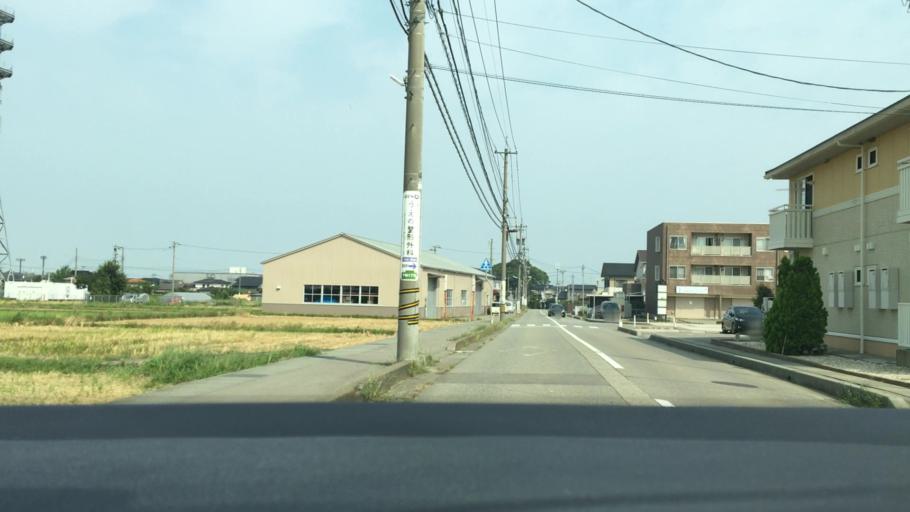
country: JP
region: Ishikawa
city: Nonoichi
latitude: 36.5185
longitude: 136.6045
